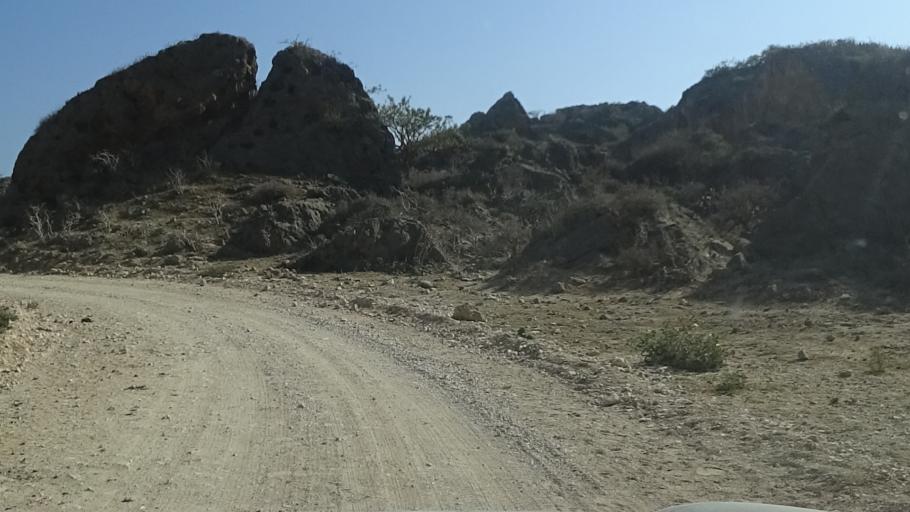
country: OM
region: Zufar
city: Salalah
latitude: 16.8438
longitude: 53.7233
